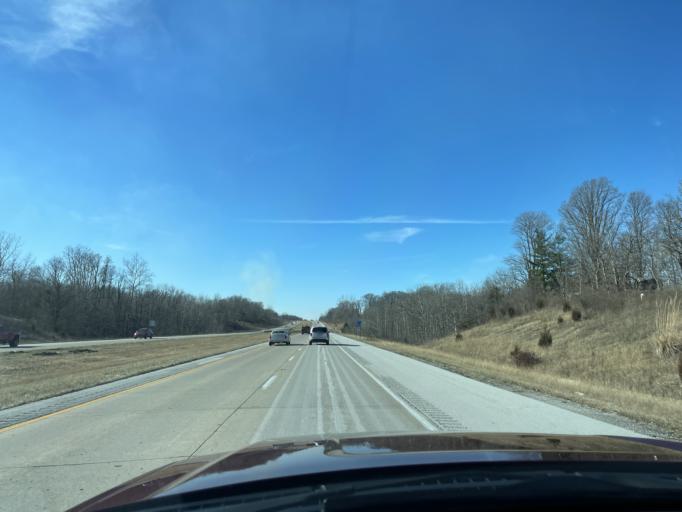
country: US
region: Indiana
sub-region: Hendricks County
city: Avon
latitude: 39.7582
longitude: -86.4442
